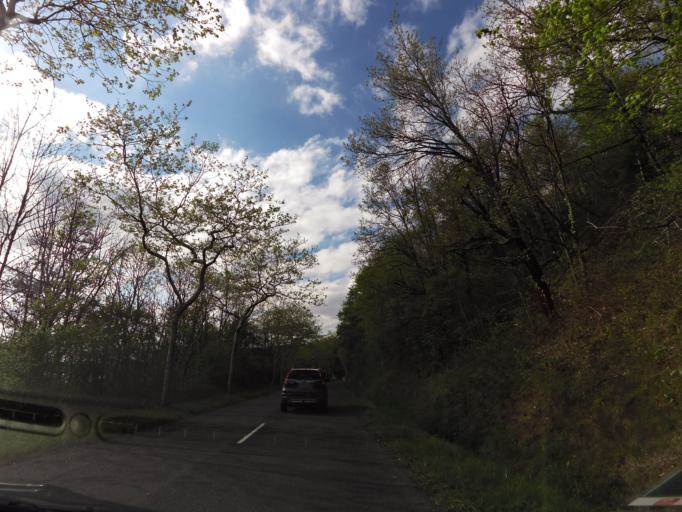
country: FR
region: Midi-Pyrenees
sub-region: Departement du Tarn
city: Soreze
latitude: 43.4334
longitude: 2.0492
